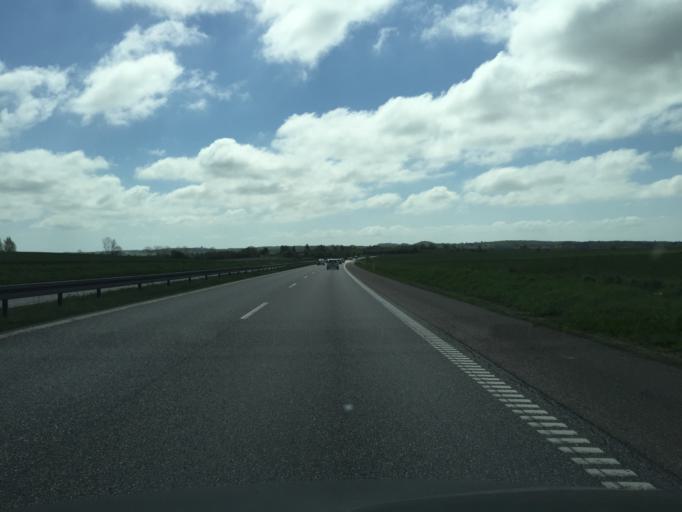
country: DK
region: Zealand
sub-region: Vordingborg Kommune
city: Orslev
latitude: 55.0490
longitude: 11.9837
